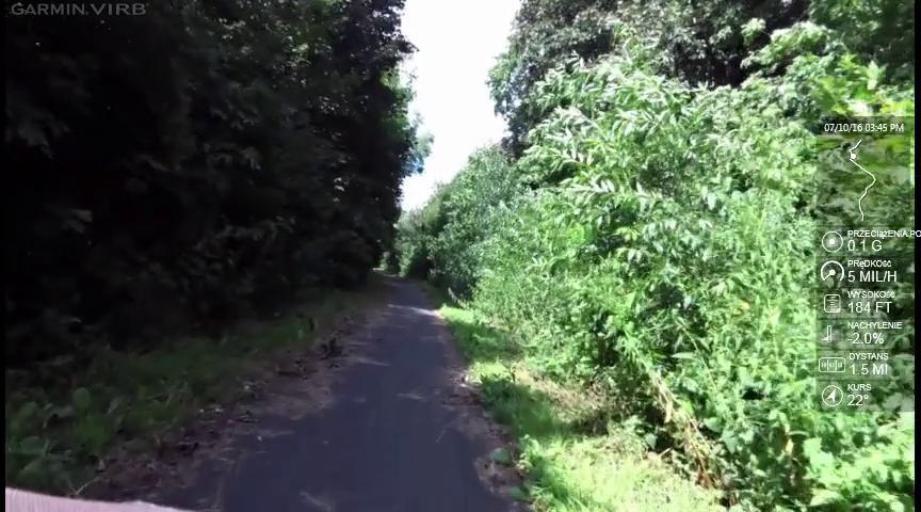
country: PL
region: West Pomeranian Voivodeship
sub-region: Powiat gryfinski
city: Banie
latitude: 53.1312
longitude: 14.6180
